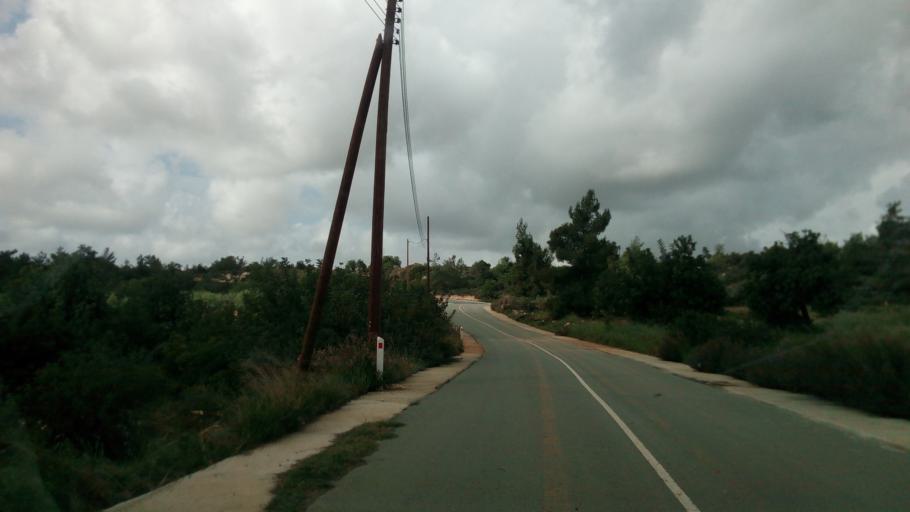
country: CY
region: Limassol
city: Sotira
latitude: 34.7296
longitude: 32.8672
